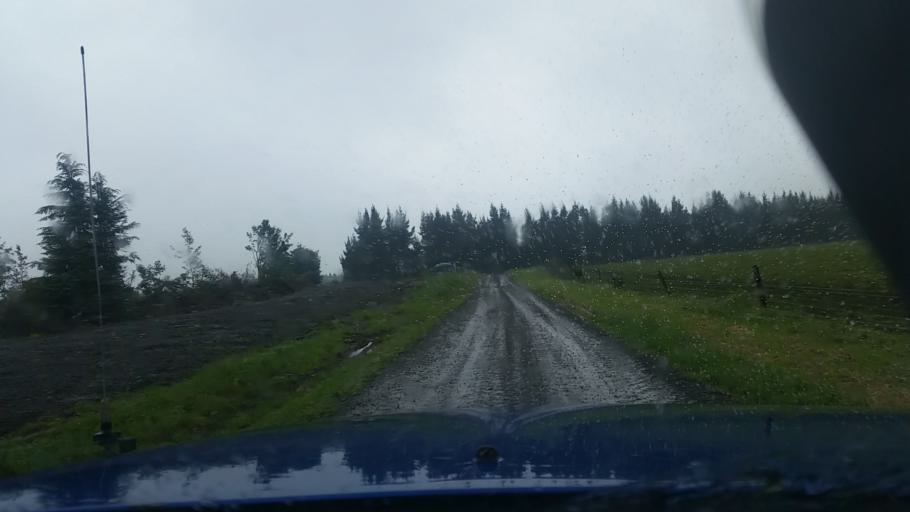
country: NZ
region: Canterbury
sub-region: Ashburton District
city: Methven
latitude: -43.5838
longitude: 171.5376
